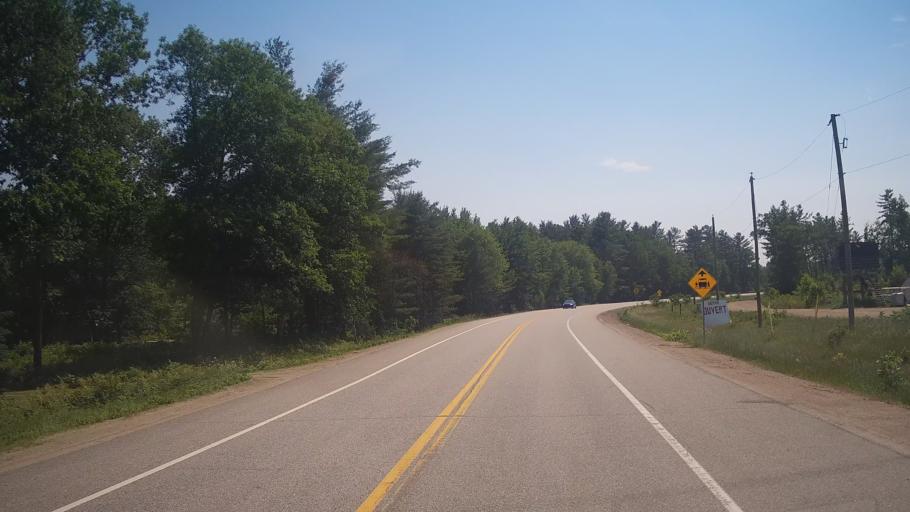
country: CA
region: Quebec
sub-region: Outaouais
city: Fort-Coulonge
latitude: 45.9084
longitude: -76.9216
